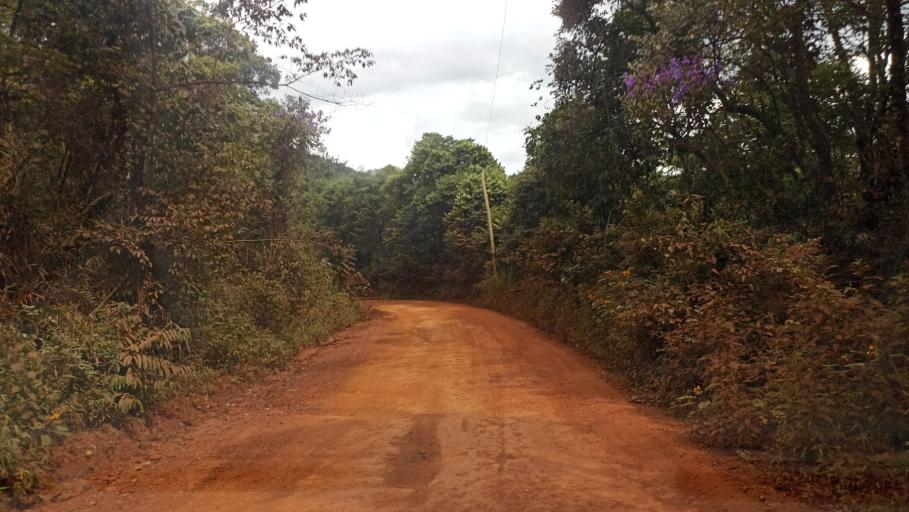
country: BR
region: Minas Gerais
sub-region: Itabirito
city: Itabirito
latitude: -20.3859
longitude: -43.7603
